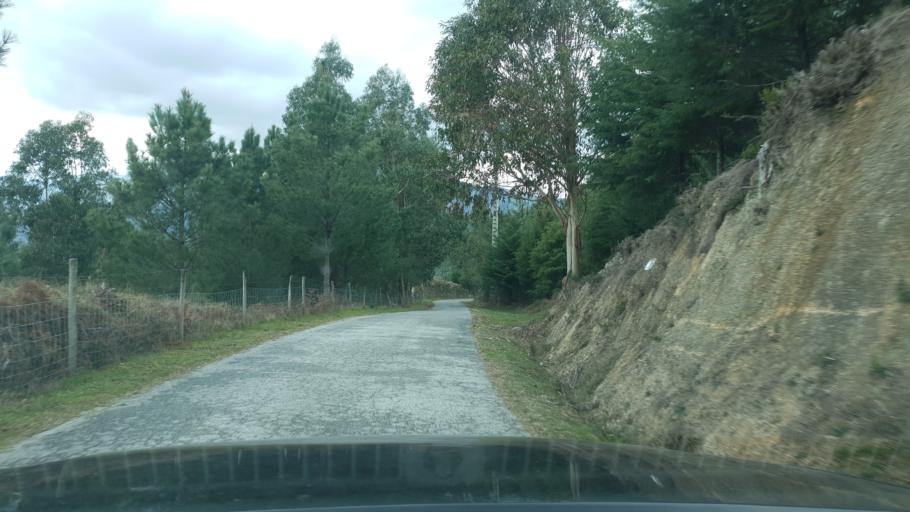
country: PT
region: Viseu
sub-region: Castro Daire
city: Castro Daire
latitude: 40.8784
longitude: -7.9921
